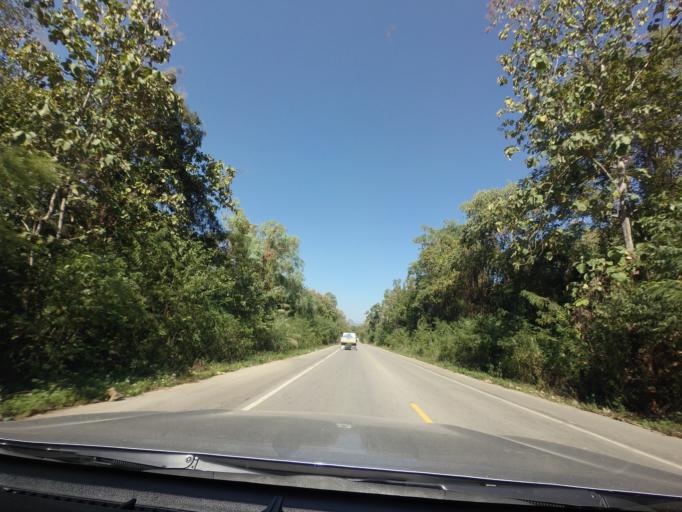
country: TH
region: Lampang
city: Mae Mo
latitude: 18.4920
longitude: 99.6449
